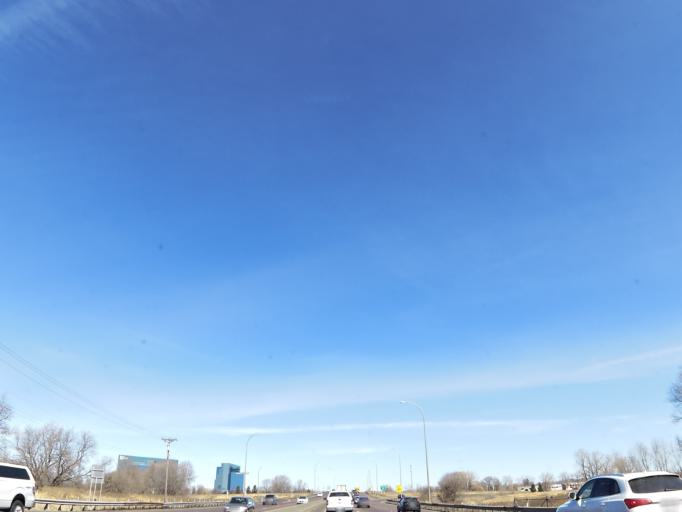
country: US
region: Minnesota
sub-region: Hennepin County
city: Minnetonka Mills
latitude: 44.9791
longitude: -93.4005
